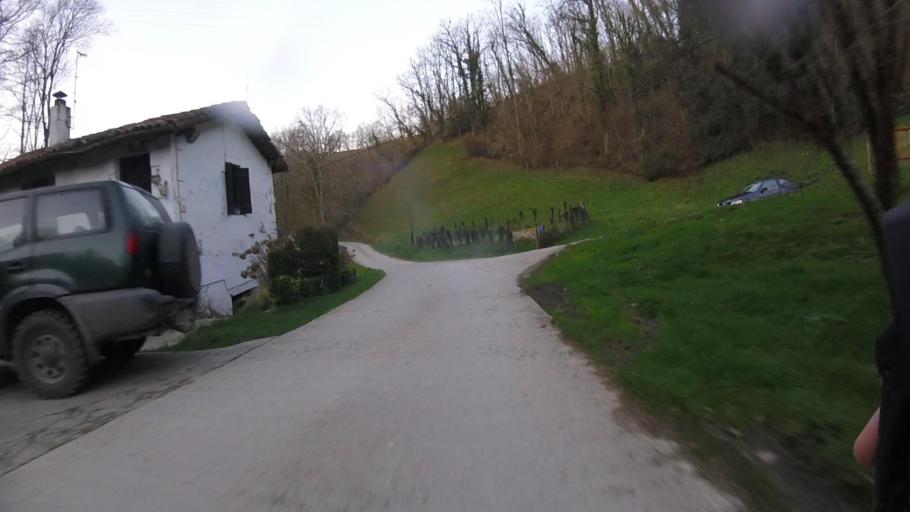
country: ES
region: Basque Country
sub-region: Provincia de Guipuzcoa
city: Errenteria
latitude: 43.2766
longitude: -1.8685
